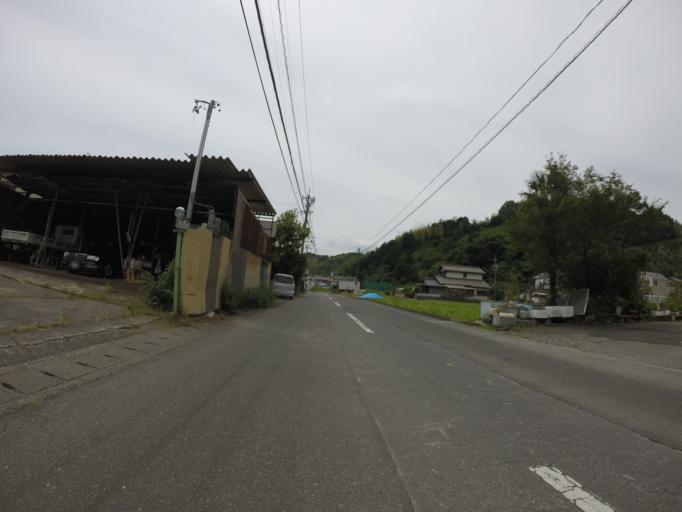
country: JP
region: Shizuoka
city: Shizuoka-shi
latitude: 35.0310
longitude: 138.4211
